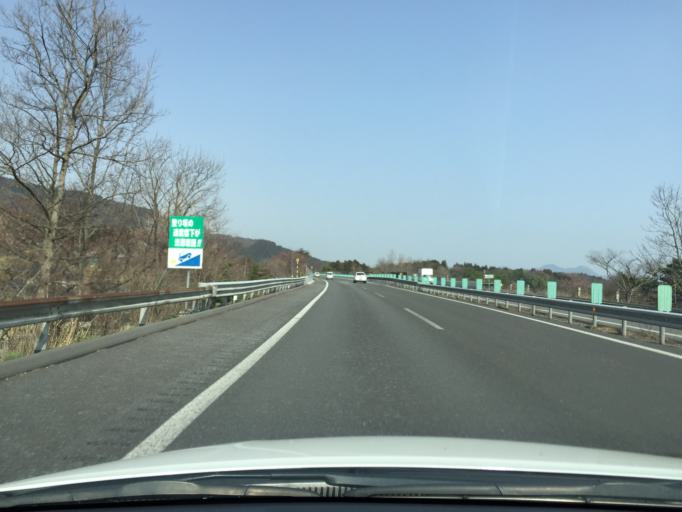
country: JP
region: Miyagi
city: Shiroishi
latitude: 37.9763
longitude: 140.6127
